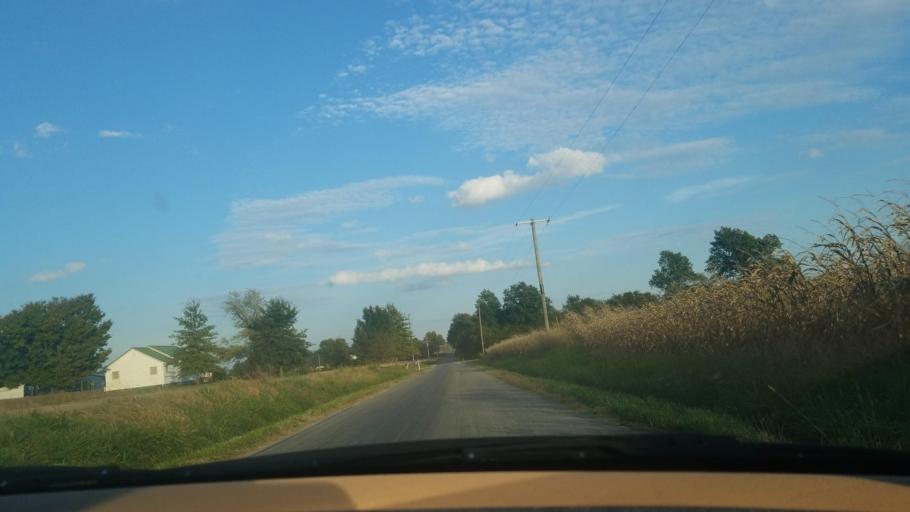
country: US
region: Illinois
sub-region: Saline County
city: Carrier Mills
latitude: 37.8050
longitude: -88.6766
